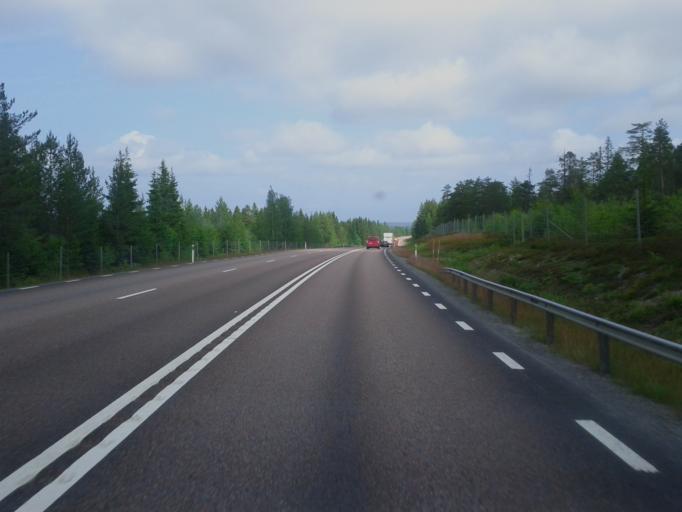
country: SE
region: Vaesterbotten
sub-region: Skelleftea Kommun
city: Burea
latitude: 64.4445
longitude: 21.2831
